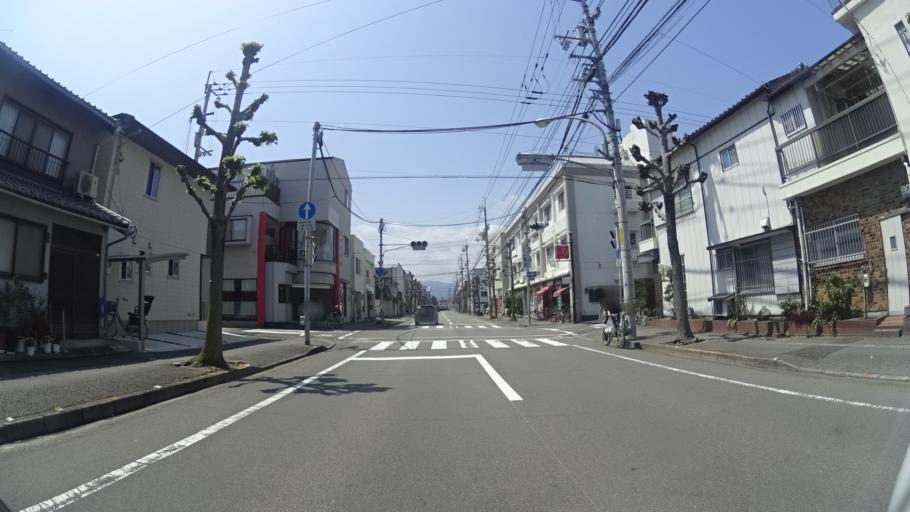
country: JP
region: Tokushima
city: Tokushima-shi
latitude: 34.0625
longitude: 134.5524
